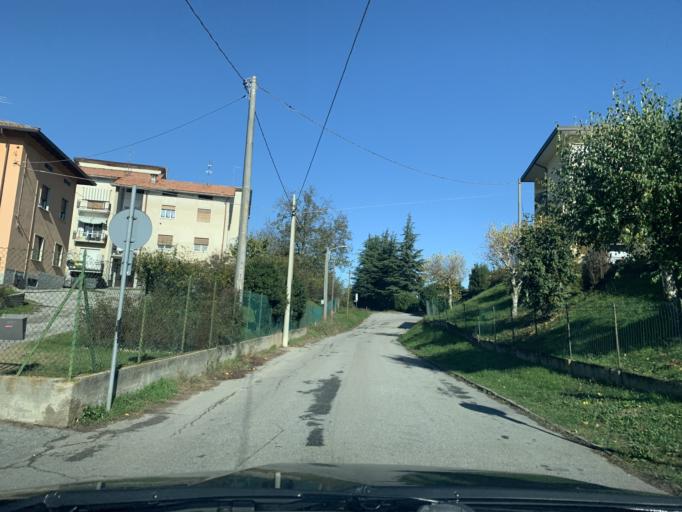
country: IT
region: Lombardy
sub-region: Provincia di Como
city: San Michele-San Giorgio
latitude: 45.6980
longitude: 9.0542
